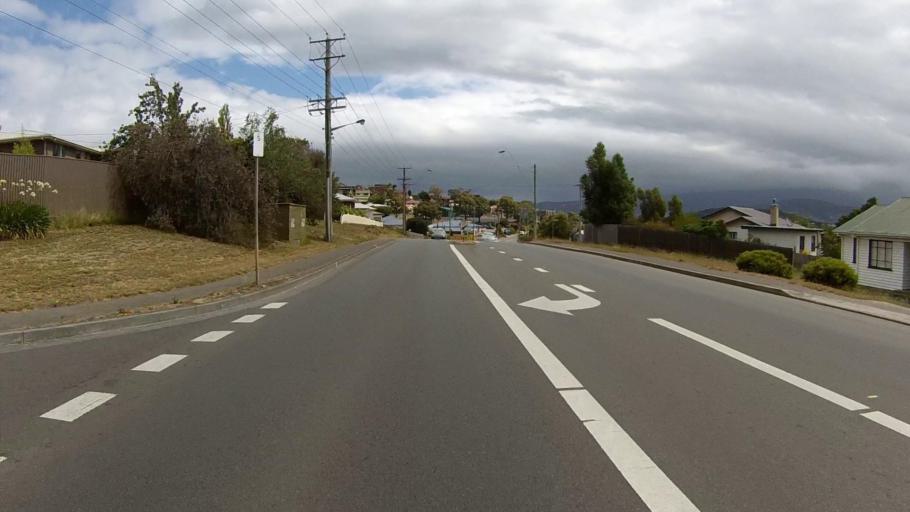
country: AU
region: Tasmania
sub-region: Clarence
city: Warrane
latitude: -42.8620
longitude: 147.3790
